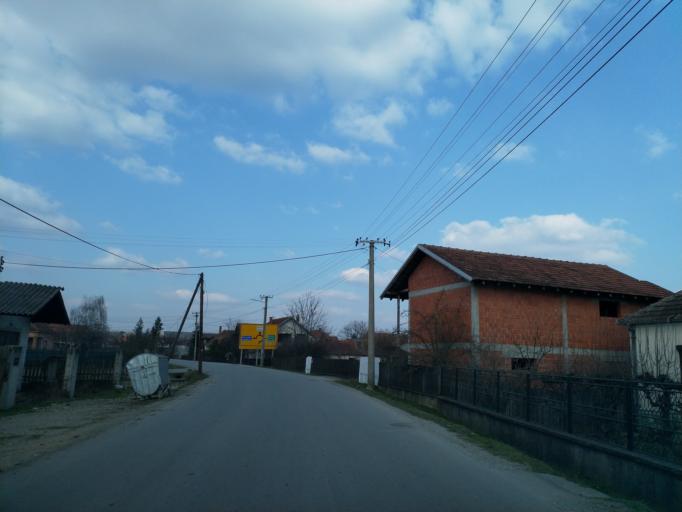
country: RS
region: Central Serbia
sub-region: Sumadijski Okrug
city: Batocina
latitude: 44.1455
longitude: 21.0770
